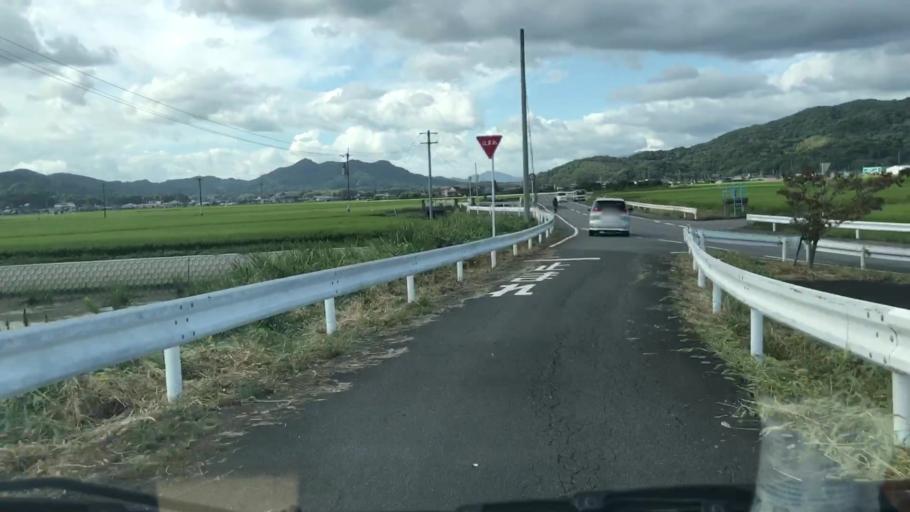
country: JP
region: Saga Prefecture
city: Kashima
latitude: 33.1135
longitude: 130.0816
